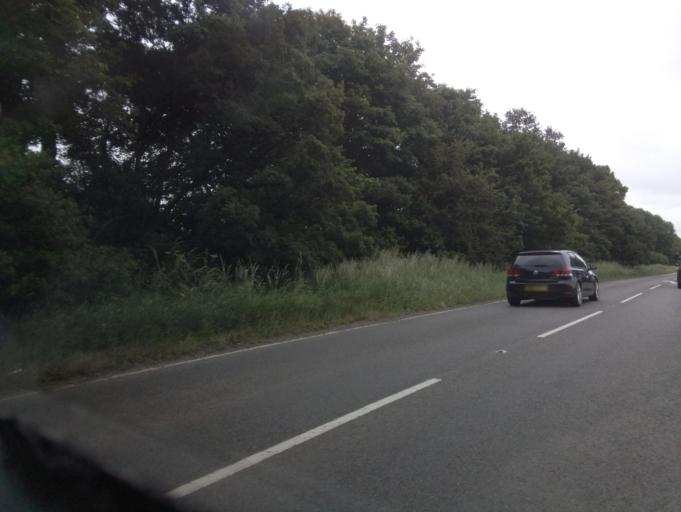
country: GB
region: England
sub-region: Leicestershire
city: Sileby
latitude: 52.8081
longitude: -1.0810
